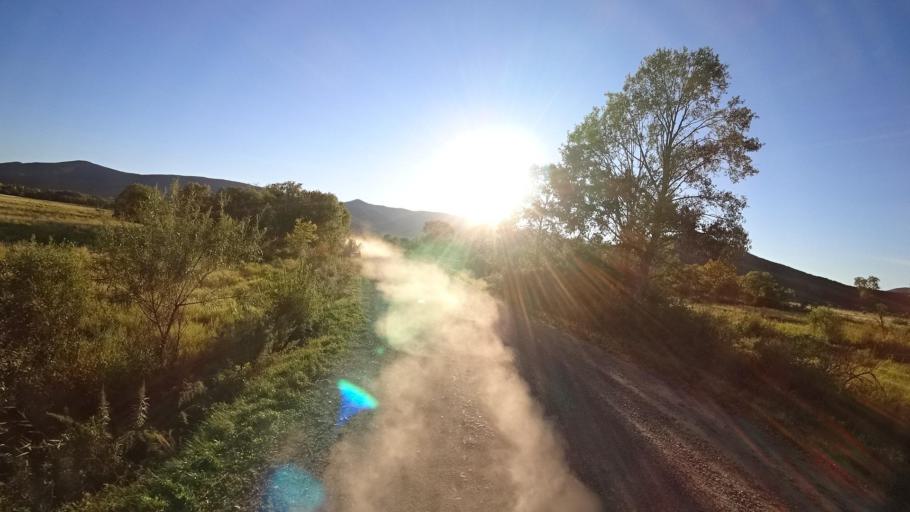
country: RU
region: Primorskiy
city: Kirovskiy
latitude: 44.8326
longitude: 133.5880
